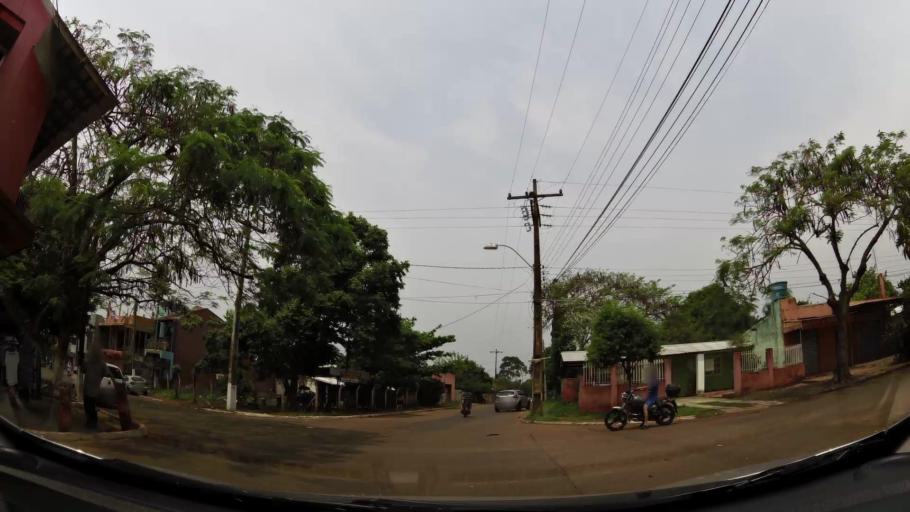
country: BR
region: Parana
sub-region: Foz Do Iguacu
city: Foz do Iguacu
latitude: -25.5660
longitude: -54.6098
